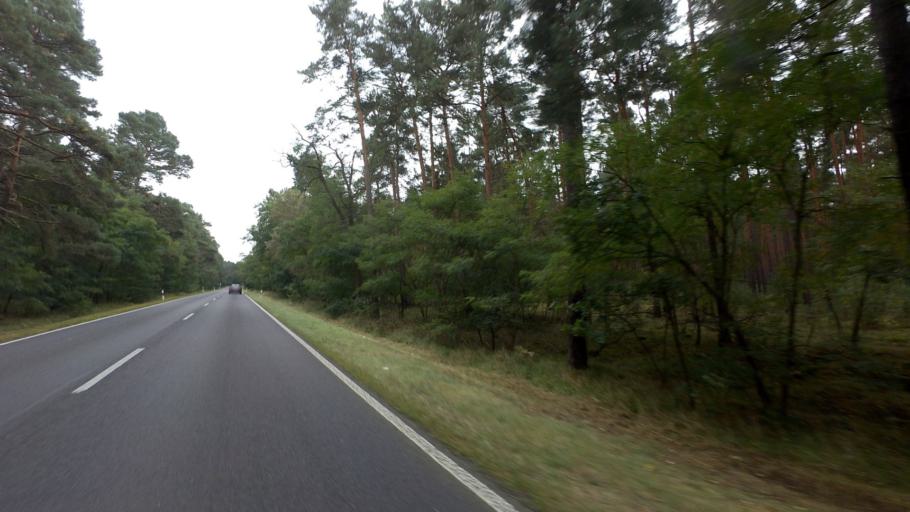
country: DE
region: Brandenburg
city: Golssen
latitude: 52.0060
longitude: 13.5542
